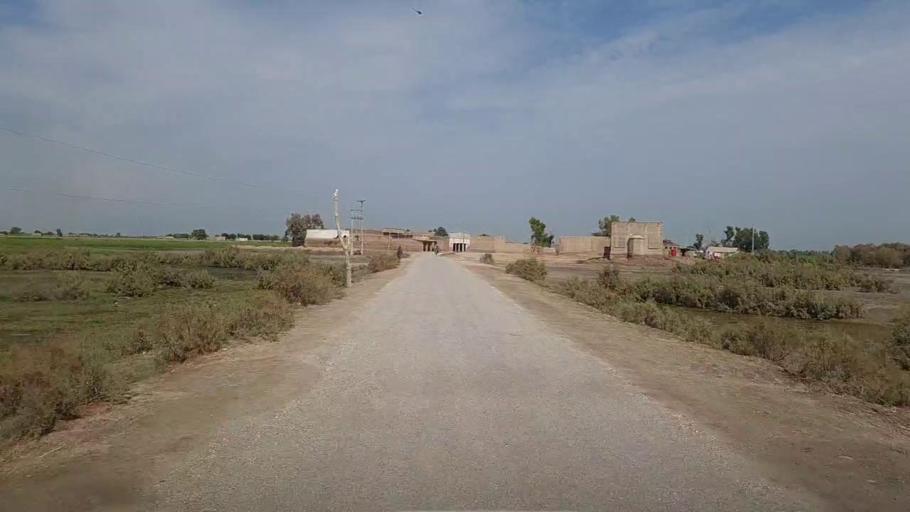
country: PK
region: Sindh
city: Thul
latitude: 28.2934
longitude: 68.8262
